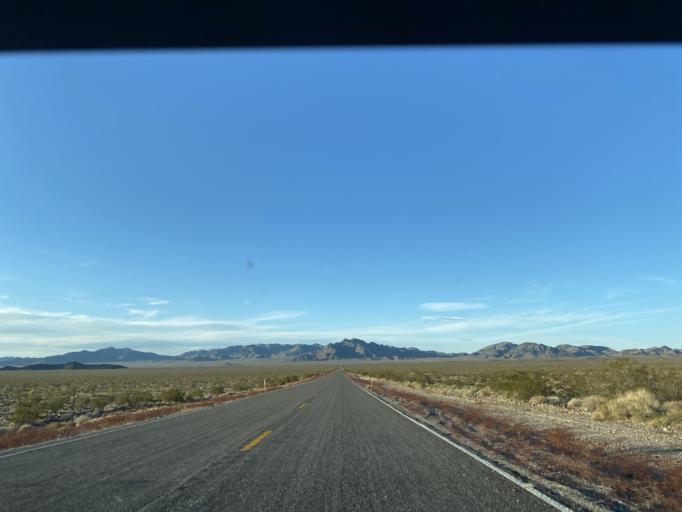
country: US
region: Nevada
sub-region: Nye County
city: Pahrump
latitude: 36.5065
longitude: -116.1180
